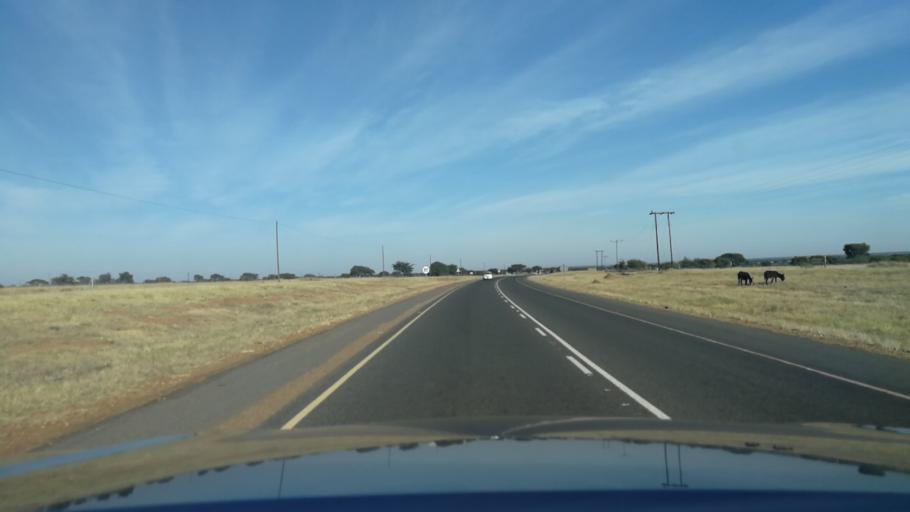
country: BW
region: South East
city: Janeng
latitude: -25.4780
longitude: 25.5124
